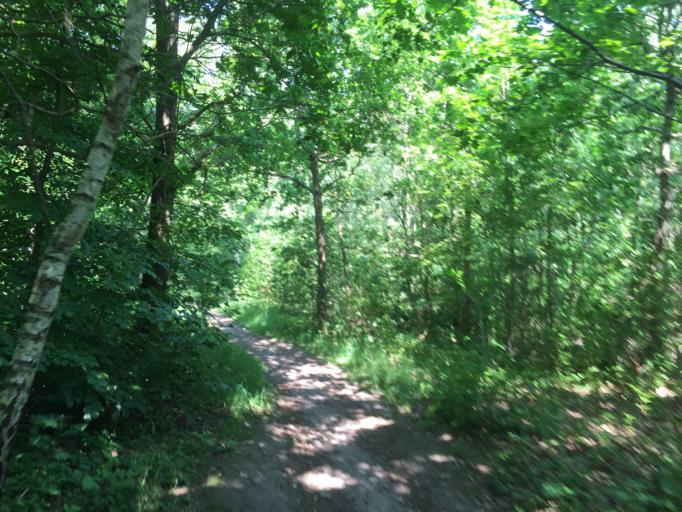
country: SE
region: Skane
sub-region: Lunds Kommun
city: Veberod
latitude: 55.6212
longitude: 13.5085
